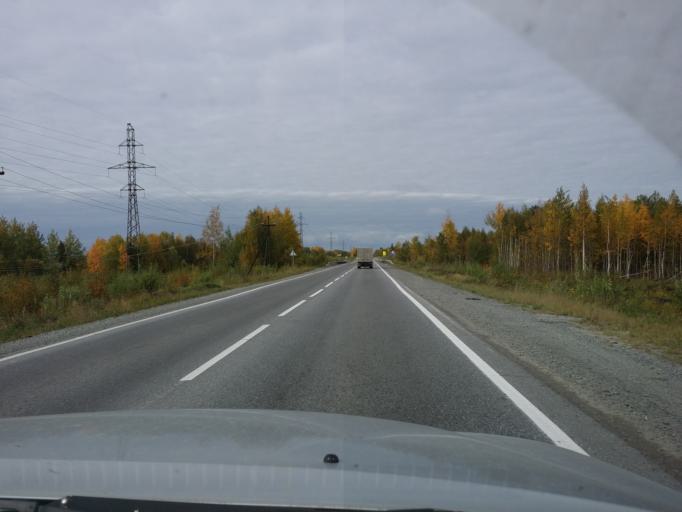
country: RU
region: Khanty-Mansiyskiy Avtonomnyy Okrug
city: Megion
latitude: 61.1032
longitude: 75.9471
